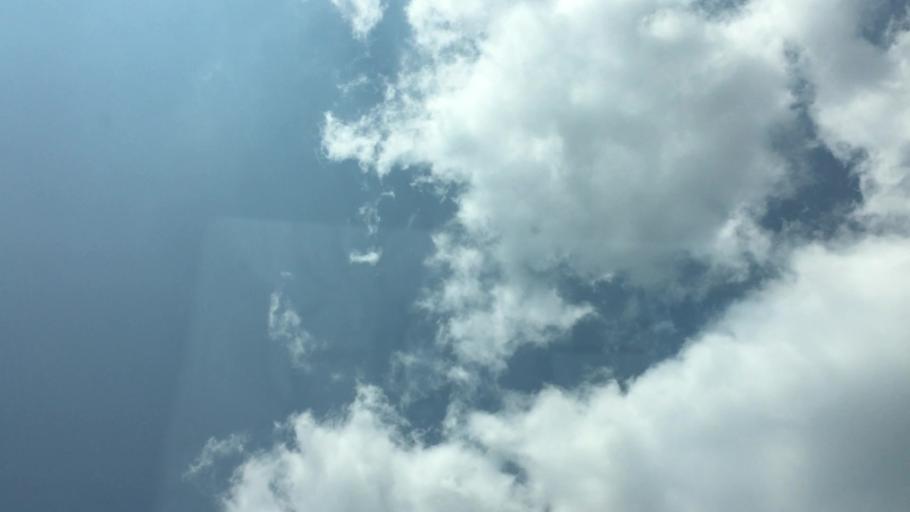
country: US
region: Alabama
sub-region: Pickens County
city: Gordo
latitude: 33.2797
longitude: -87.7855
